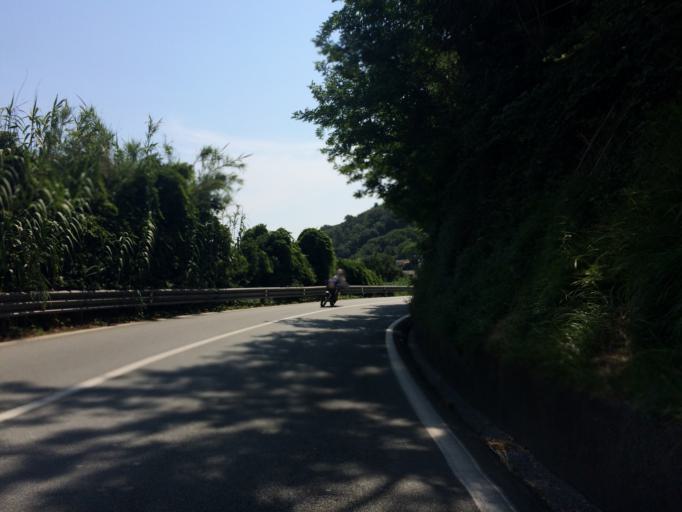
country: IT
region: Liguria
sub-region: Provincia di Genova
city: Arenzano
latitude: 44.4015
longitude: 8.6776
